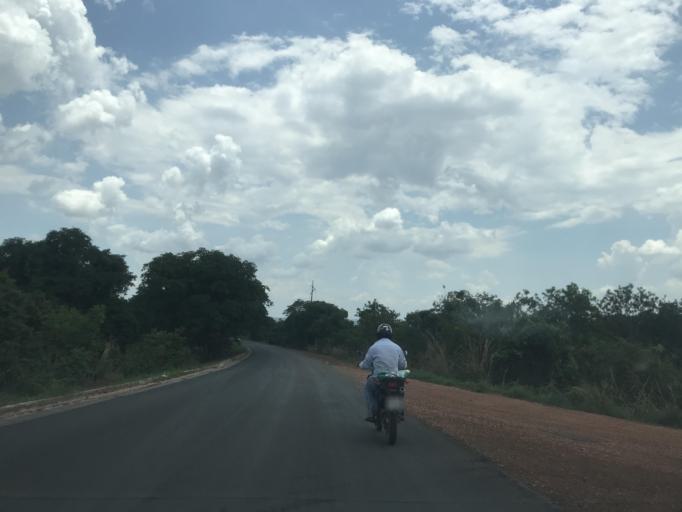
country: BR
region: Goias
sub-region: Bela Vista De Goias
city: Bela Vista de Goias
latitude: -17.0366
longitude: -48.6608
